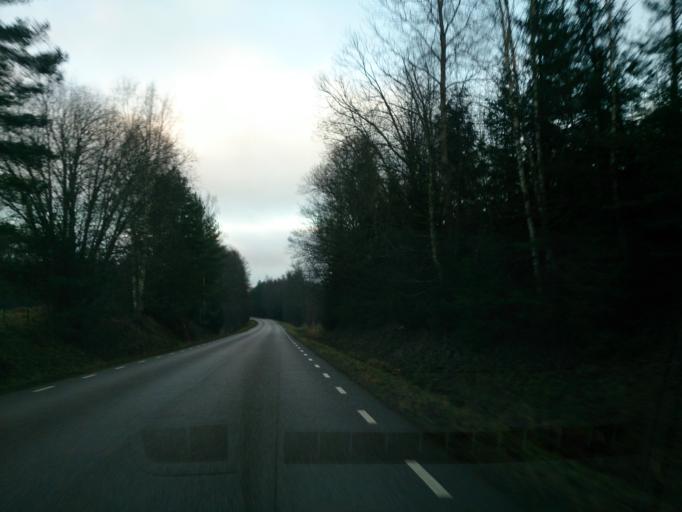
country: SE
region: OEstergoetland
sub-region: Atvidabergs Kommun
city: Atvidaberg
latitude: 58.2547
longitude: 16.0212
